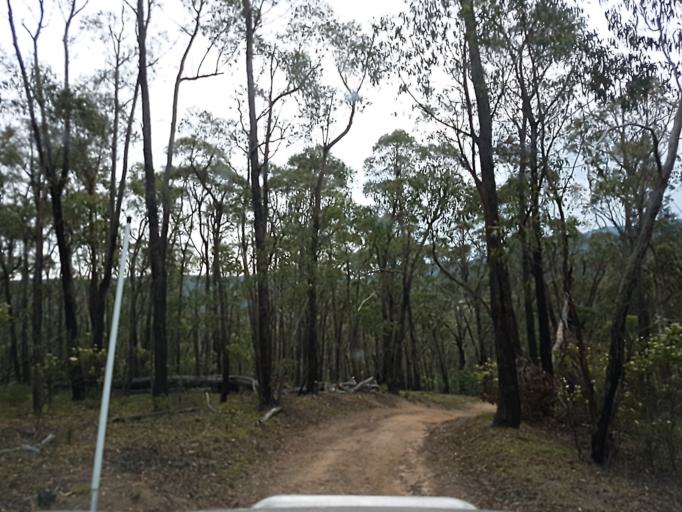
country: AU
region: New South Wales
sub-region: Snowy River
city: Jindabyne
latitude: -36.8703
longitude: 148.3290
